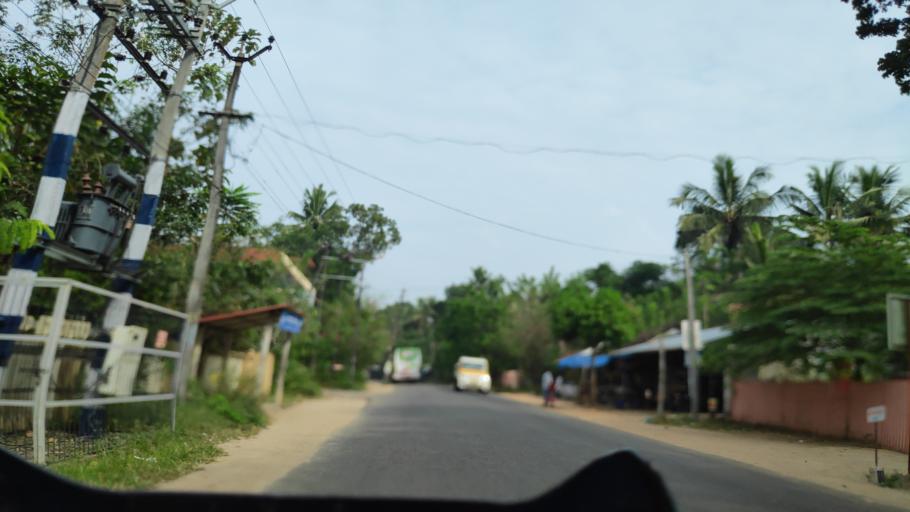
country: IN
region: Kerala
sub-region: Alappuzha
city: Kutiatodu
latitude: 9.8105
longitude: 76.3528
